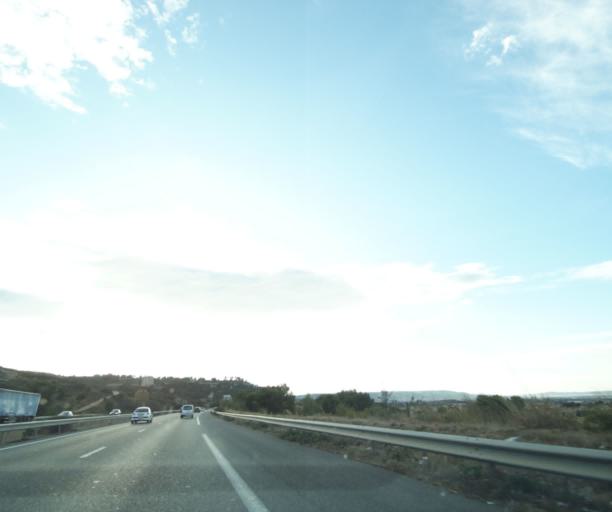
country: FR
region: Provence-Alpes-Cote d'Azur
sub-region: Departement des Bouches-du-Rhone
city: Gignac-la-Nerthe
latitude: 43.3867
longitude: 5.2413
